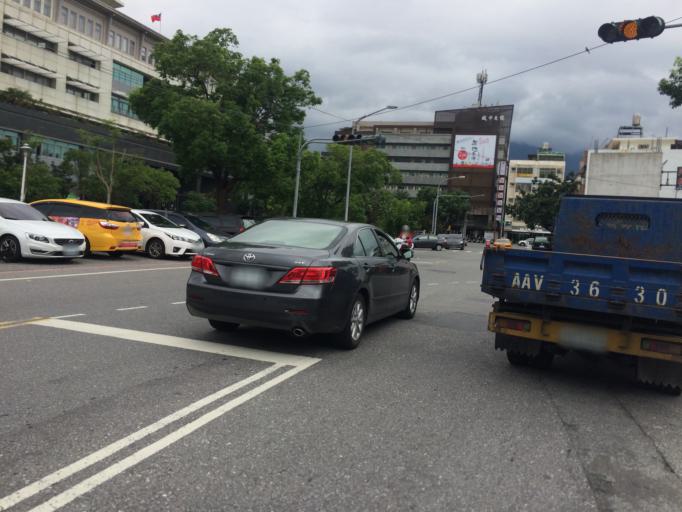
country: TW
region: Taiwan
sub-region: Hualien
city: Hualian
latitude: 23.9842
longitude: 121.6071
